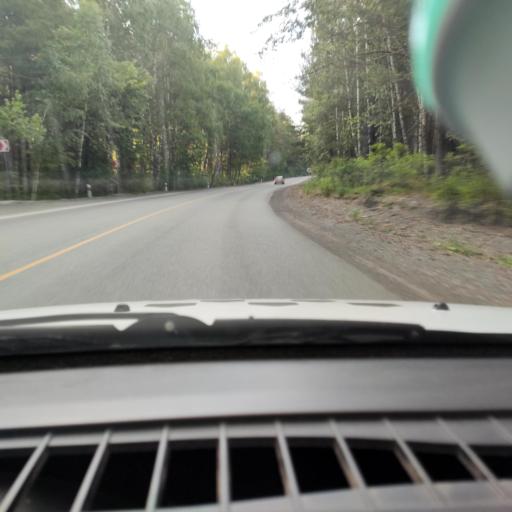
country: RU
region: Chelyabinsk
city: Turgoyak
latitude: 55.2549
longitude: 60.1987
